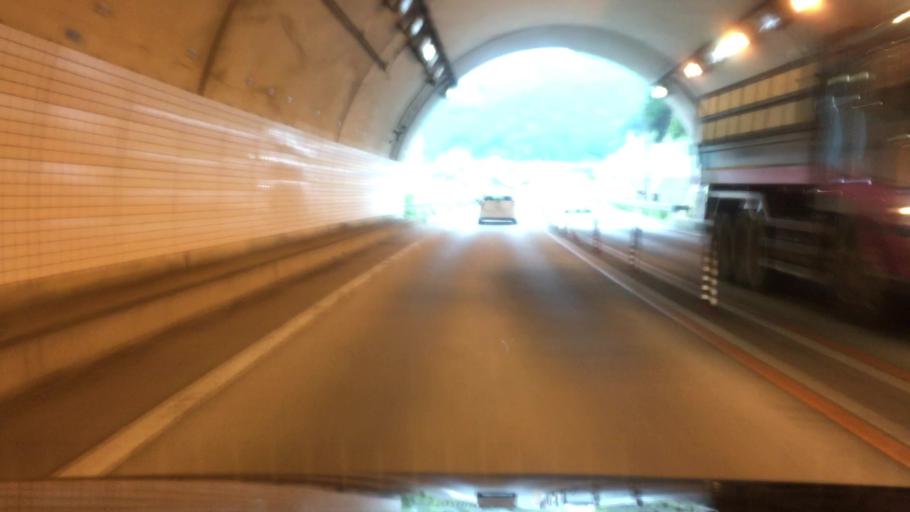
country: JP
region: Kyoto
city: Fukuchiyama
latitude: 35.2780
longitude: 134.9894
